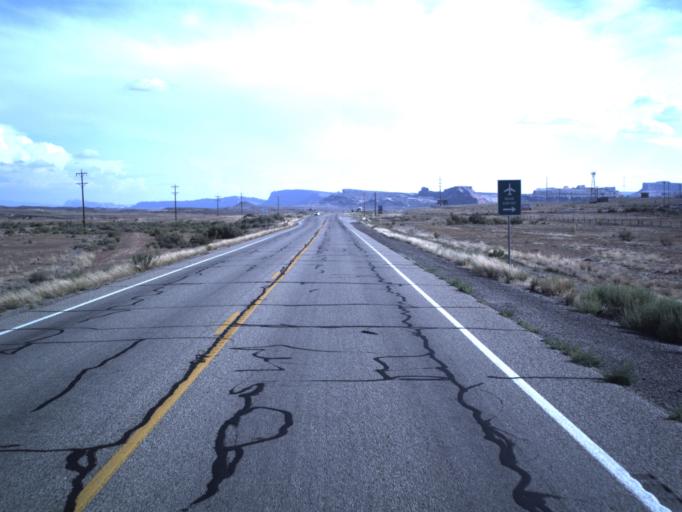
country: US
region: Utah
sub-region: Grand County
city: Moab
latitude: 38.7647
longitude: -109.7440
